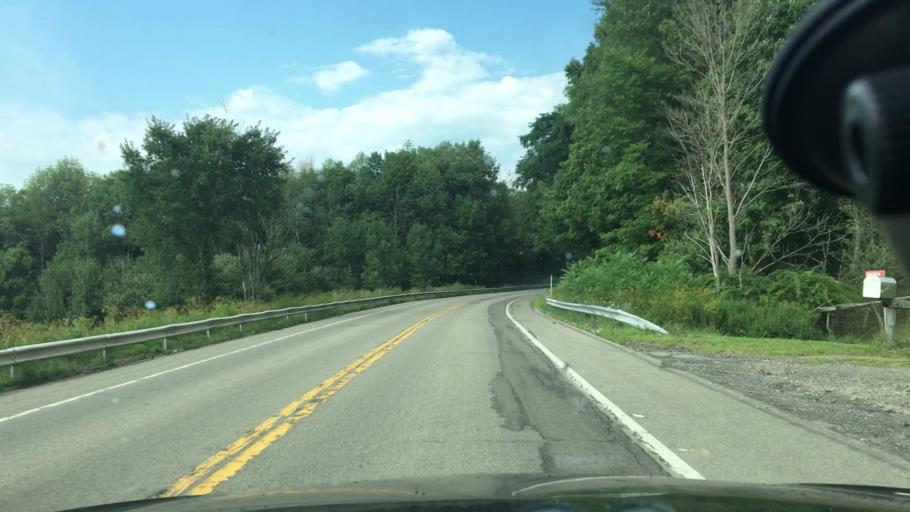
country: US
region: New York
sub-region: Cattaraugus County
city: Randolph
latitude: 42.1974
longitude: -78.8981
